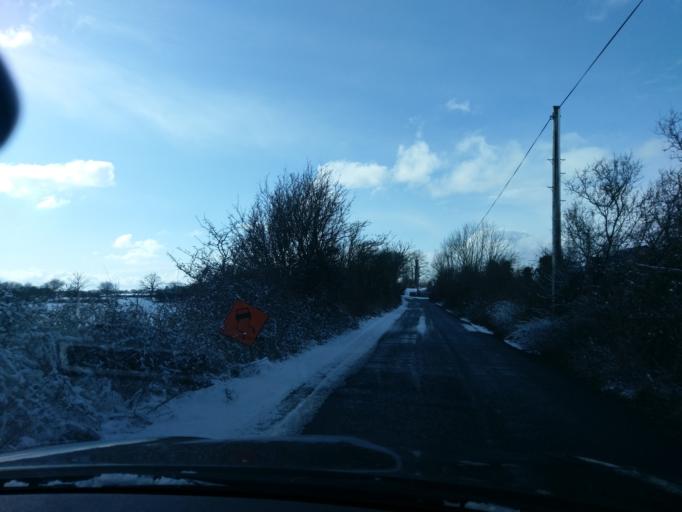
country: IE
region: Connaught
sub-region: County Galway
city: Athenry
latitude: 53.2039
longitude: -8.7725
